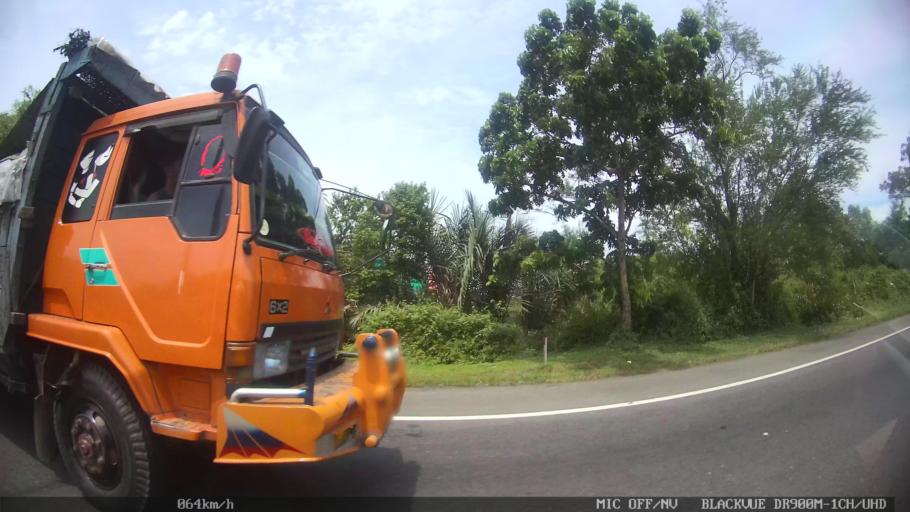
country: ID
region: North Sumatra
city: Labuhan Deli
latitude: 3.7331
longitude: 98.6804
